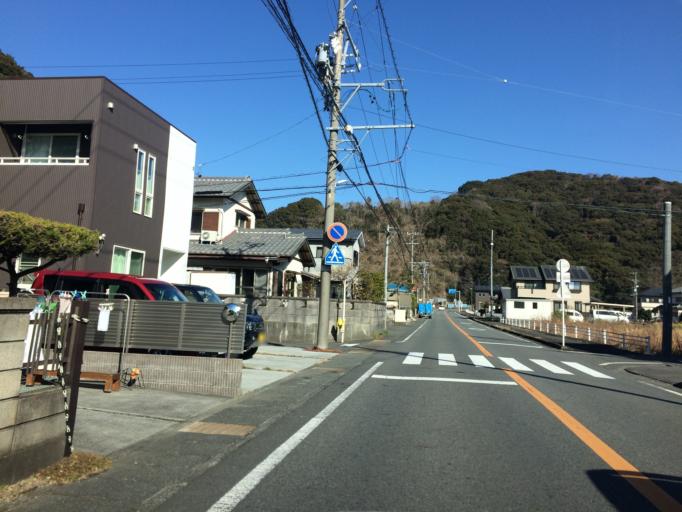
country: JP
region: Shizuoka
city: Shimada
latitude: 34.8457
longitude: 138.1979
